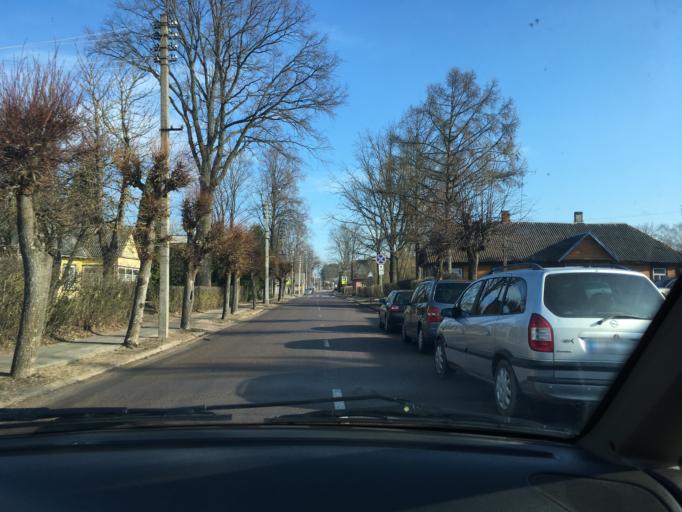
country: LT
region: Panevezys
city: Rokiskis
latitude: 55.7492
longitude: 25.8428
